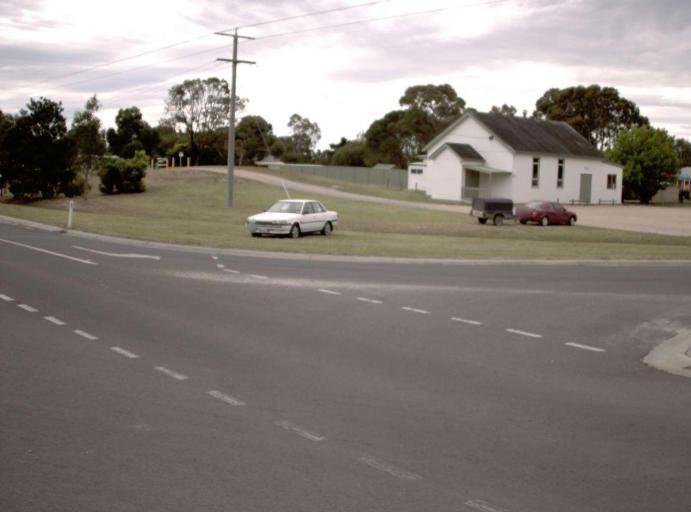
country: AU
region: Victoria
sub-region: Wellington
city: Sale
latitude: -38.1627
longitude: 147.0861
